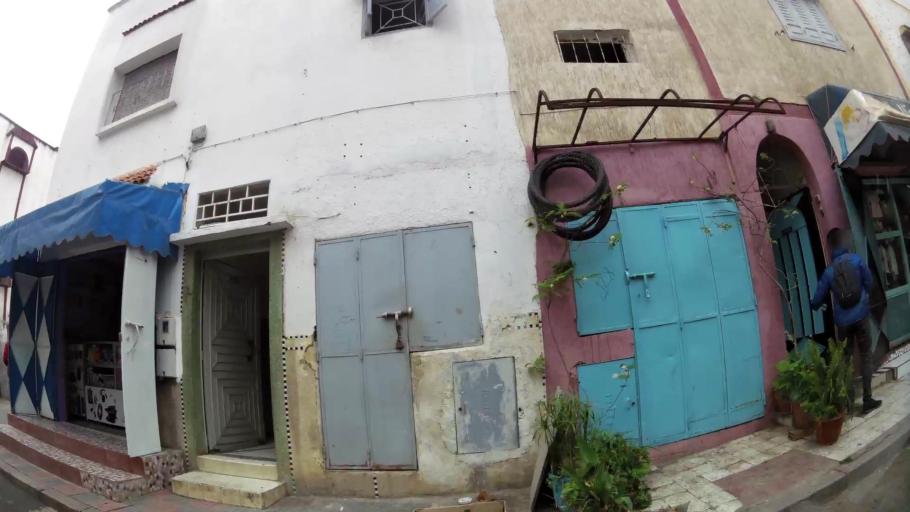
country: MA
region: Rabat-Sale-Zemmour-Zaer
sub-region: Rabat
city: Rabat
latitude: 33.9708
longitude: -6.8210
